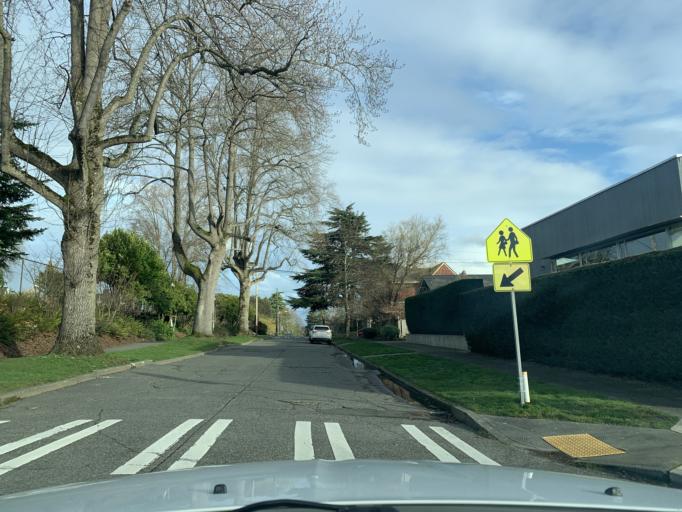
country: US
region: Washington
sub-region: King County
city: Seattle
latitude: 47.6703
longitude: -122.2926
